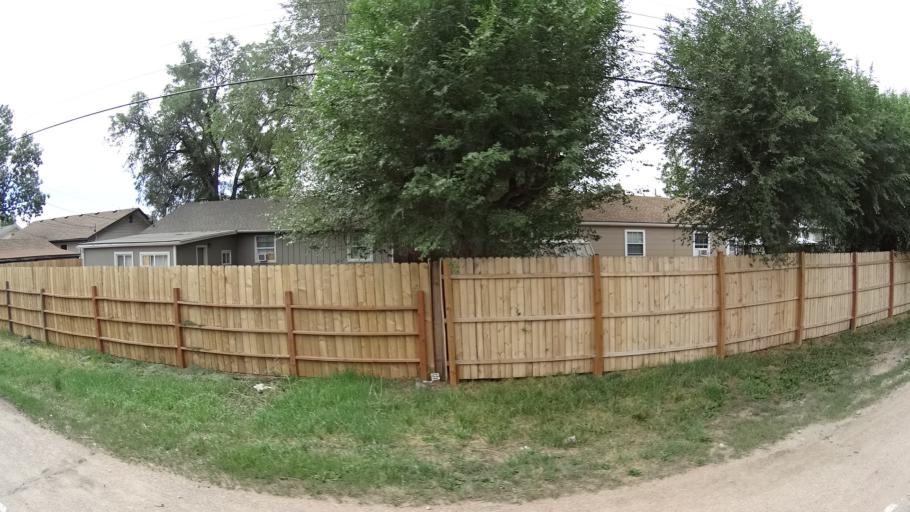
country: US
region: Colorado
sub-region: El Paso County
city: Fountain
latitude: 38.6786
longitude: -104.7087
